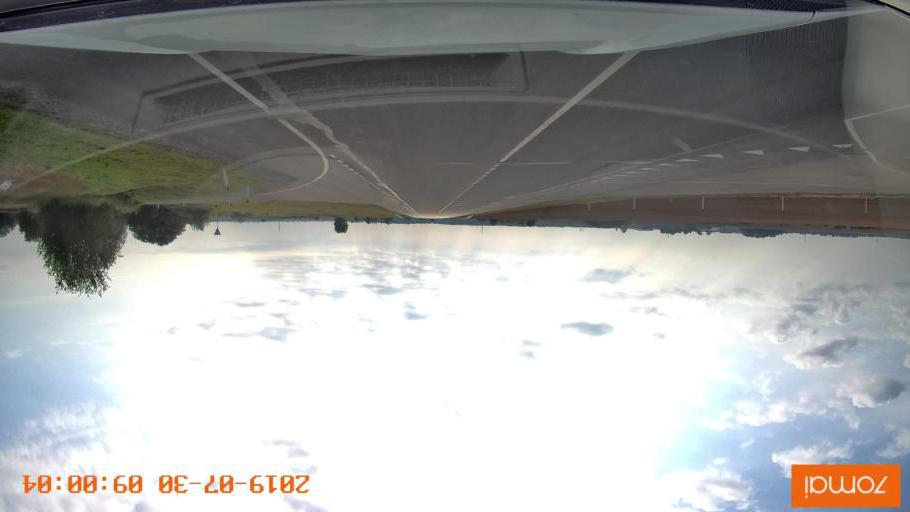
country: RU
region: Kaliningrad
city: Gusev
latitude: 54.6148
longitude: 22.1713
